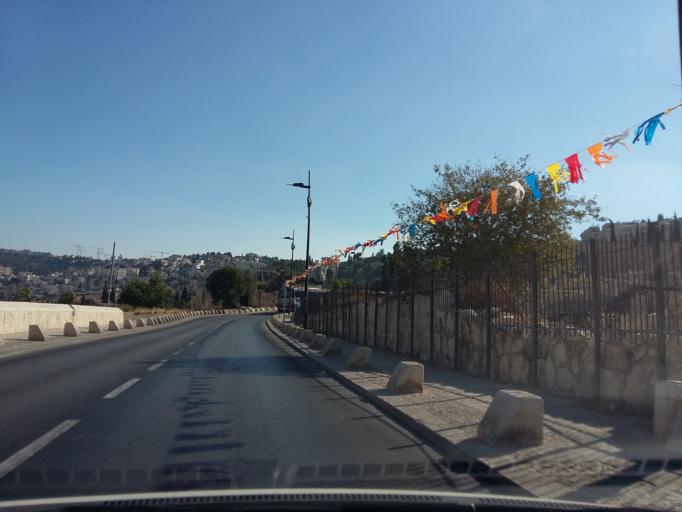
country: PS
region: West Bank
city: Old City
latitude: 31.7755
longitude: 35.2374
